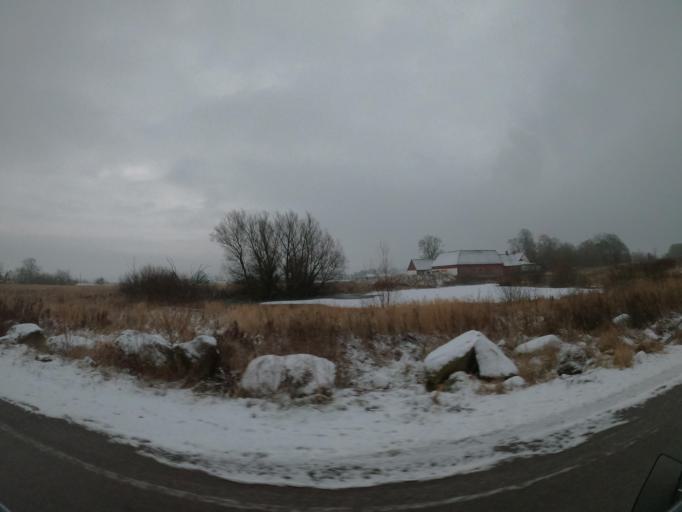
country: SE
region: Skane
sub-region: Svedala Kommun
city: Svedala
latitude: 55.5115
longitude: 13.2630
